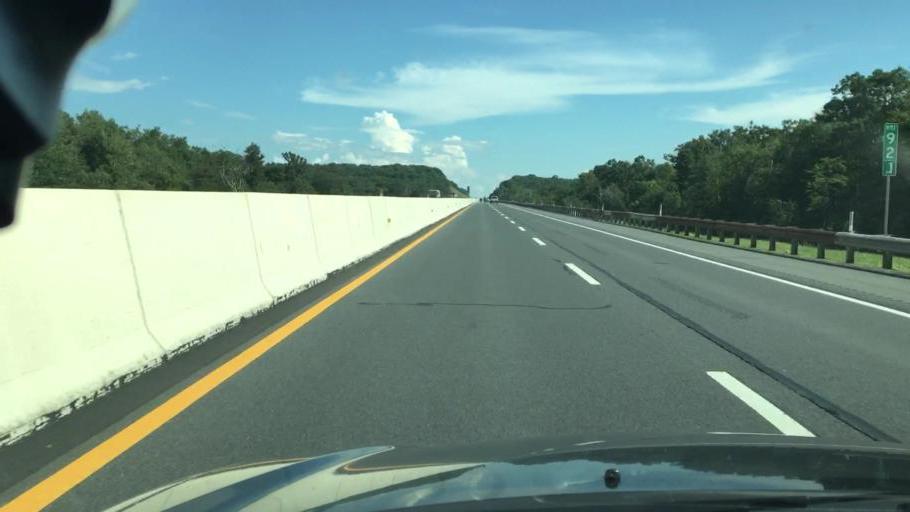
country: US
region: Pennsylvania
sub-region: Carbon County
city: Towamensing Trails
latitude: 41.0473
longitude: -75.6716
